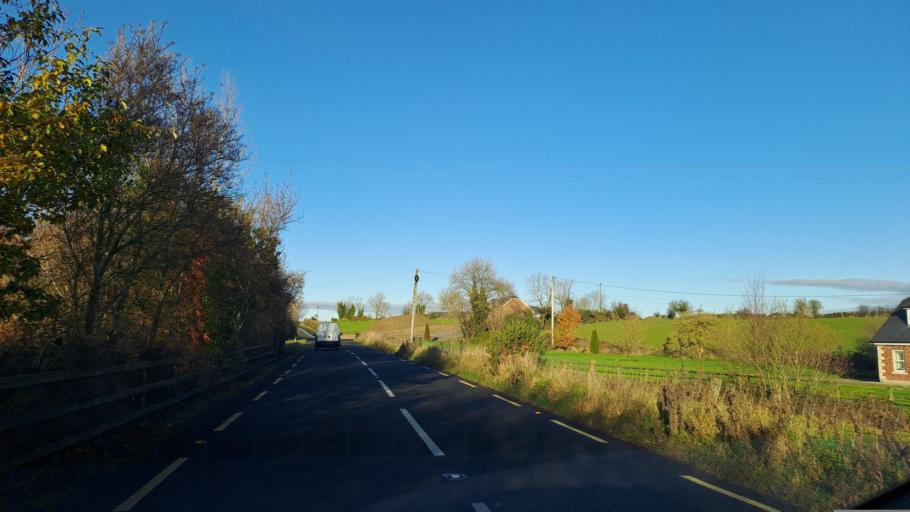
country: IE
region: Ulster
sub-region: An Cabhan
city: Mullagh
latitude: 53.8300
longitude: -6.9524
